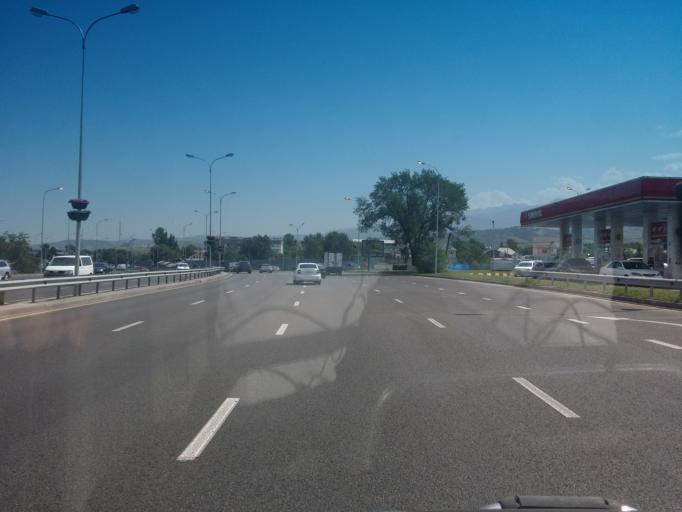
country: KZ
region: Almaty Qalasy
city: Almaty
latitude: 43.1946
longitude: 76.8942
